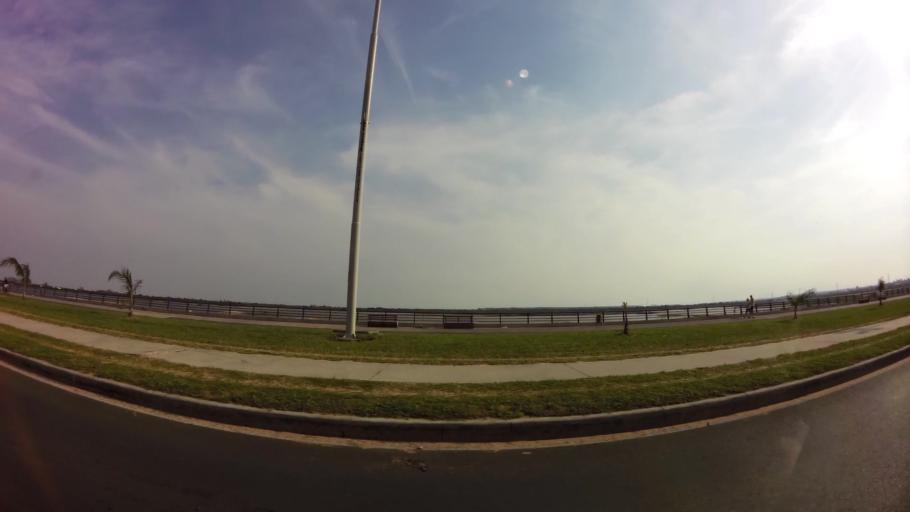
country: PY
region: Asuncion
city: Asuncion
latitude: -25.2765
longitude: -57.6240
